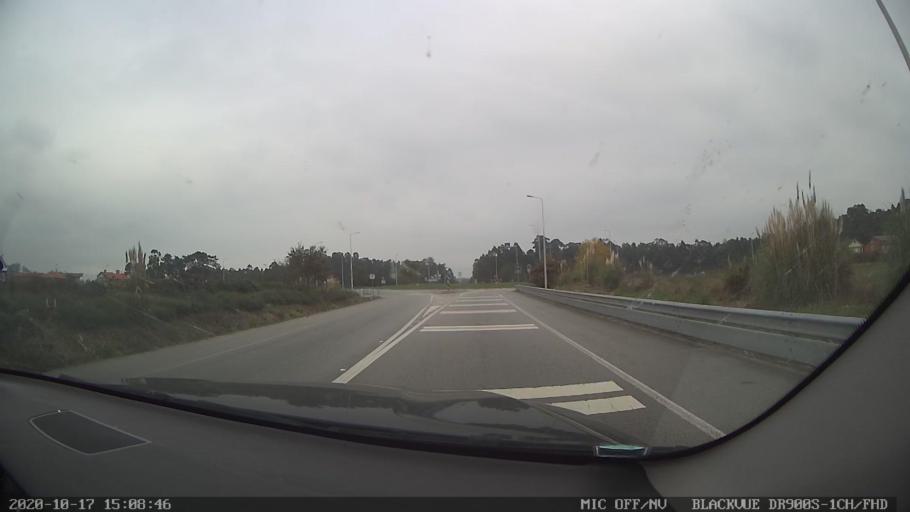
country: PT
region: Braga
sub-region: Esposende
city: Esposende
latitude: 41.5292
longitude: -8.7383
